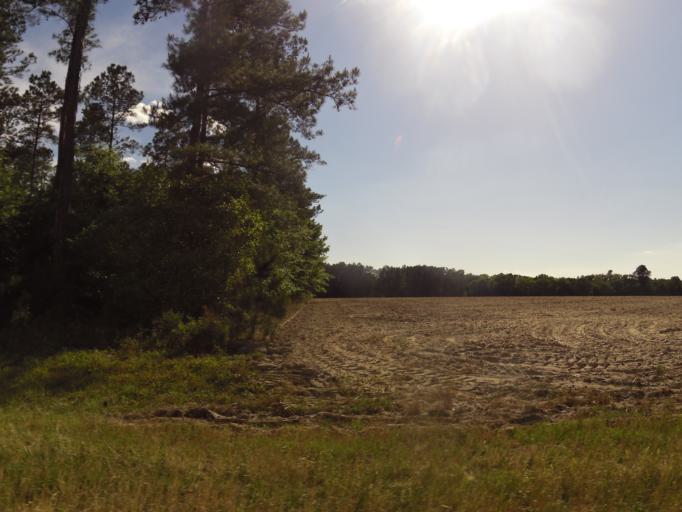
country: US
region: South Carolina
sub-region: Allendale County
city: Fairfax
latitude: 33.0195
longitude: -81.2172
